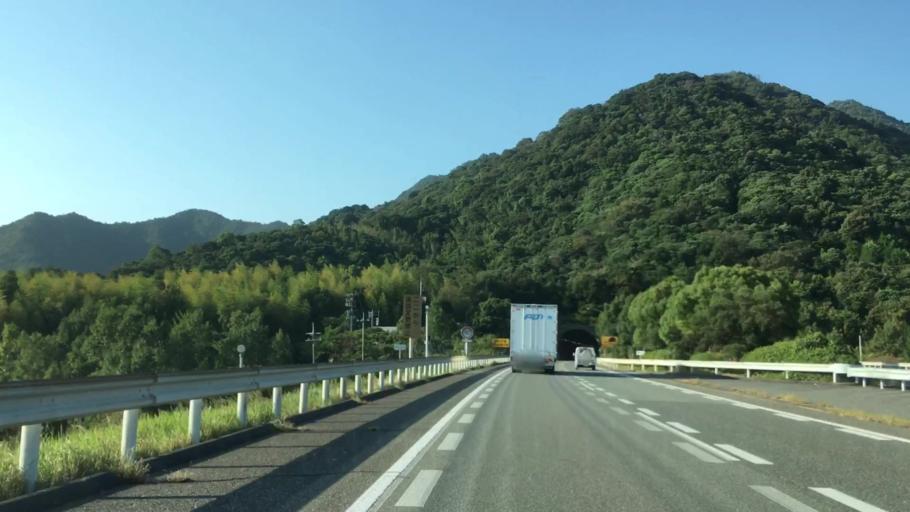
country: JP
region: Yamaguchi
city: Ogori-shimogo
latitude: 34.0990
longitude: 131.4515
